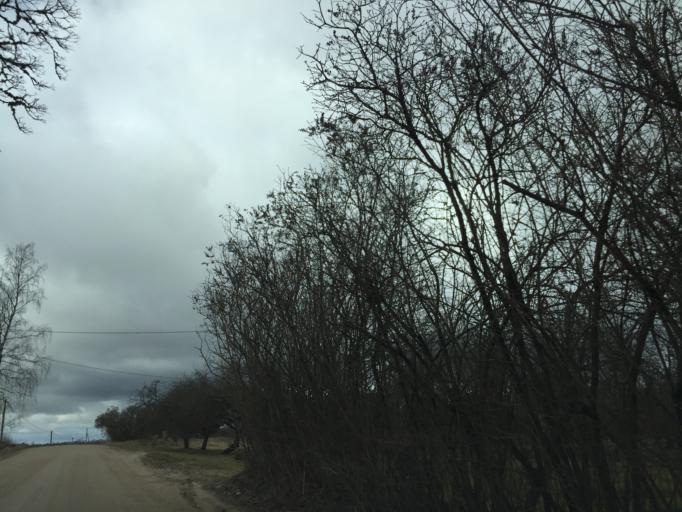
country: LV
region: Ilukste
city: Ilukste
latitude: 56.0673
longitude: 26.0871
